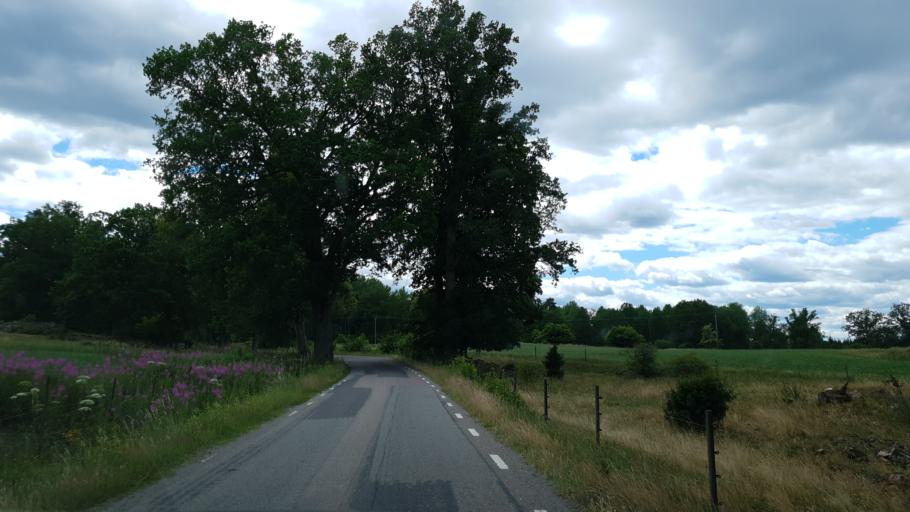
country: SE
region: Kalmar
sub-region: Hultsfreds Kommun
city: Virserum
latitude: 57.0584
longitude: 15.5894
